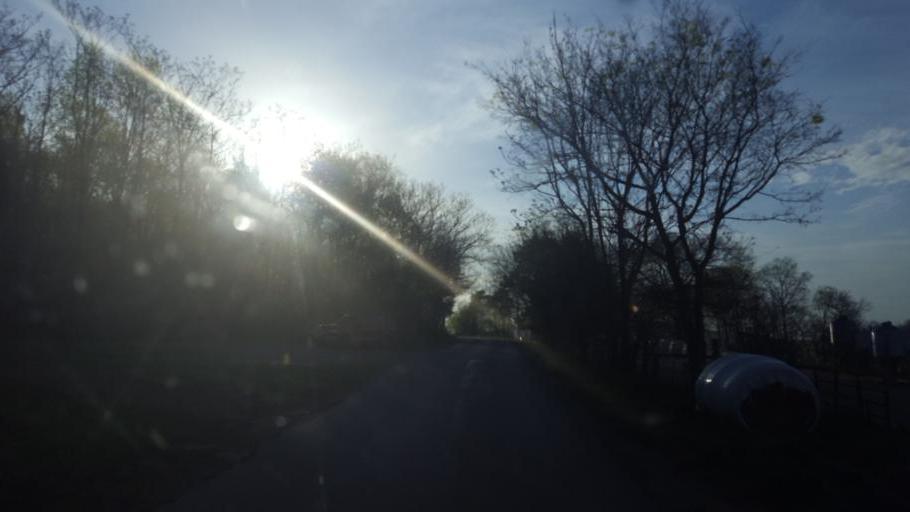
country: US
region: Kentucky
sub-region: Hart County
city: Munfordville
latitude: 37.2432
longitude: -85.9062
